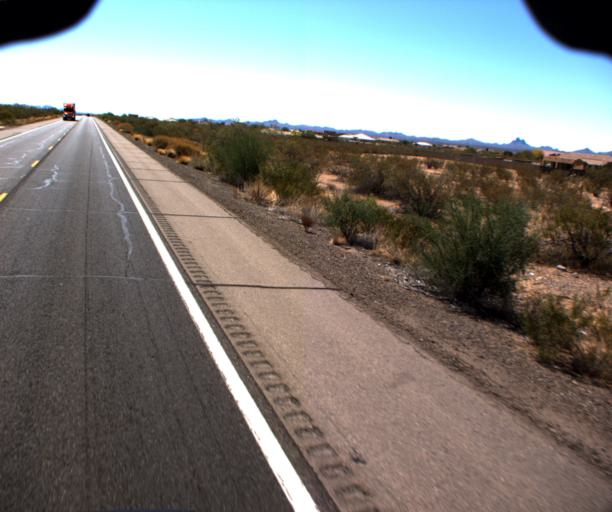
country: US
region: Arizona
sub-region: Yavapai County
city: Congress
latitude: 34.0424
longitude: -112.8343
